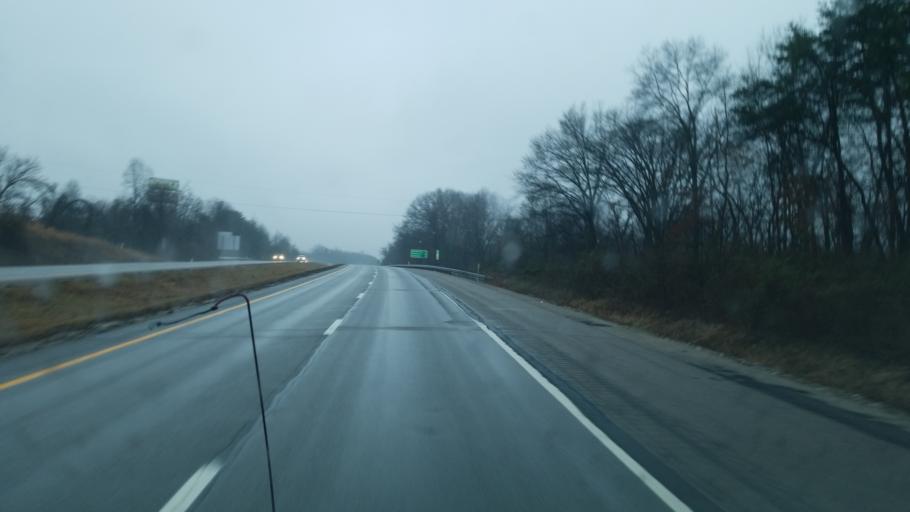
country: US
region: West Virginia
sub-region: Wood County
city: Williamstown
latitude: 39.3767
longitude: -81.4403
